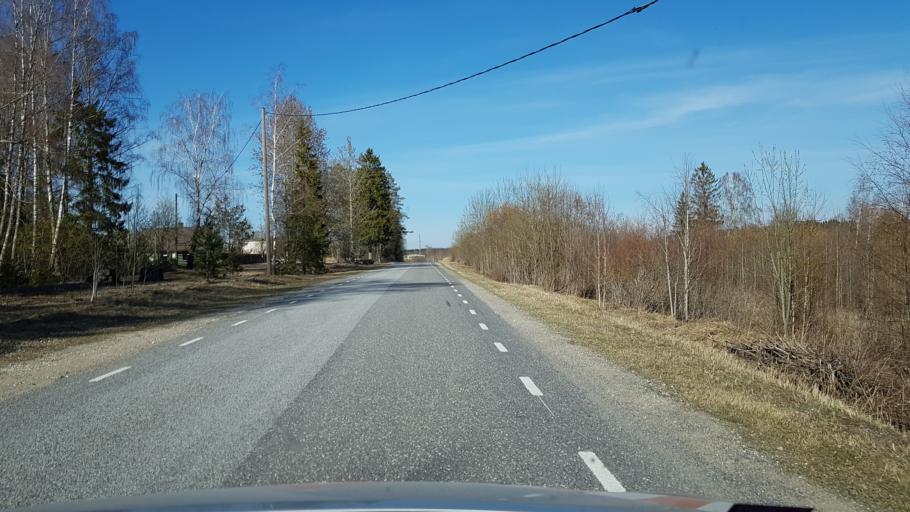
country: EE
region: Laeaene-Virumaa
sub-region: Rakke vald
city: Rakke
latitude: 58.9903
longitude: 26.2689
